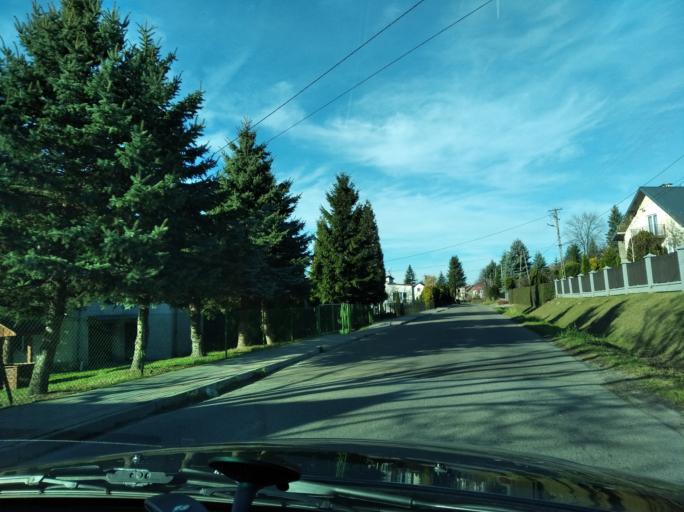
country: PL
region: Subcarpathian Voivodeship
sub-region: Powiat rzeszowski
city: Lutoryz
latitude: 49.9652
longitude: 21.9153
